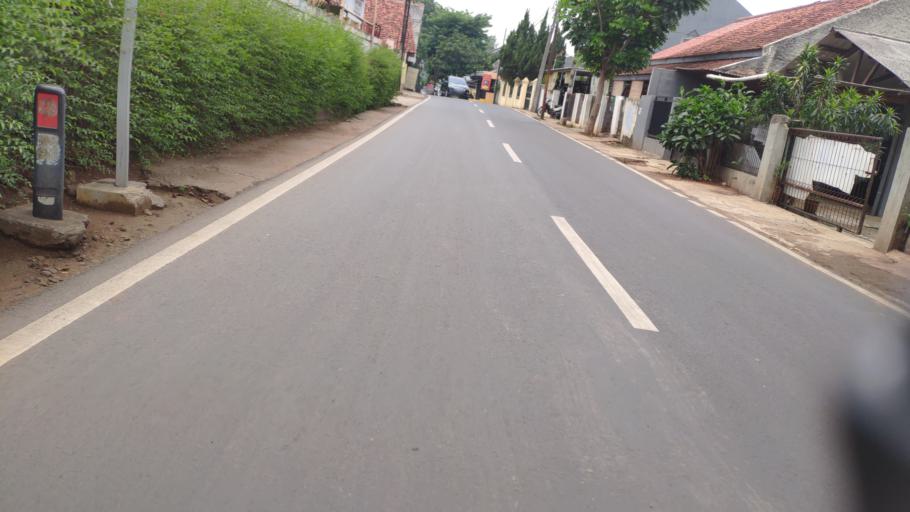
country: ID
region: West Java
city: Depok
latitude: -6.3470
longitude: 106.8207
